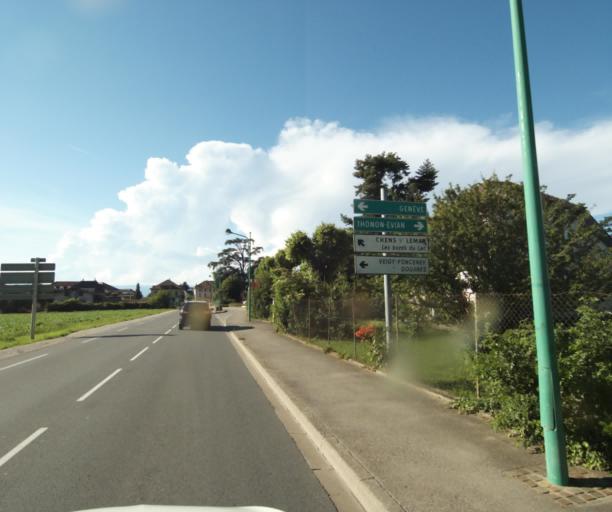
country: FR
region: Rhone-Alpes
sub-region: Departement de la Haute-Savoie
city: Douvaine
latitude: 46.3040
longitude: 6.3023
